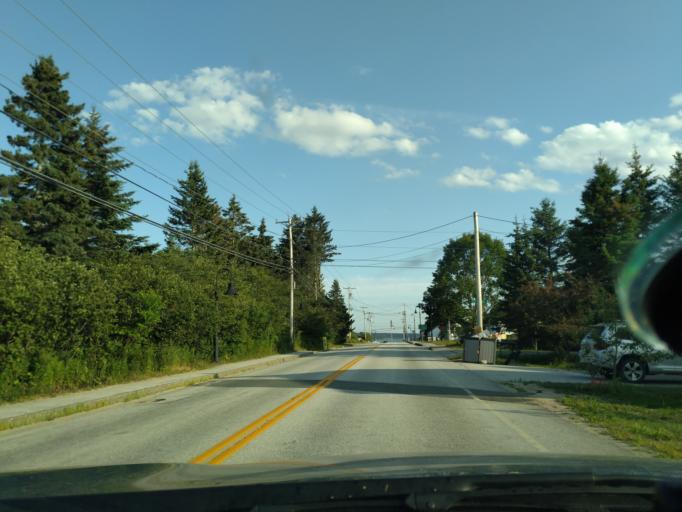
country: US
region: Maine
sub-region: Hancock County
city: Gouldsboro
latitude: 44.3971
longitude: -68.0848
